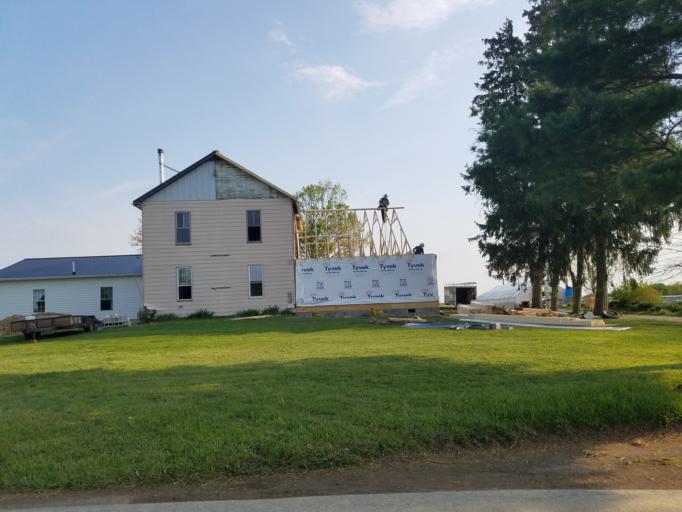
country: US
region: Ohio
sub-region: Knox County
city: Fredericktown
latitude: 40.4957
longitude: -82.6139
